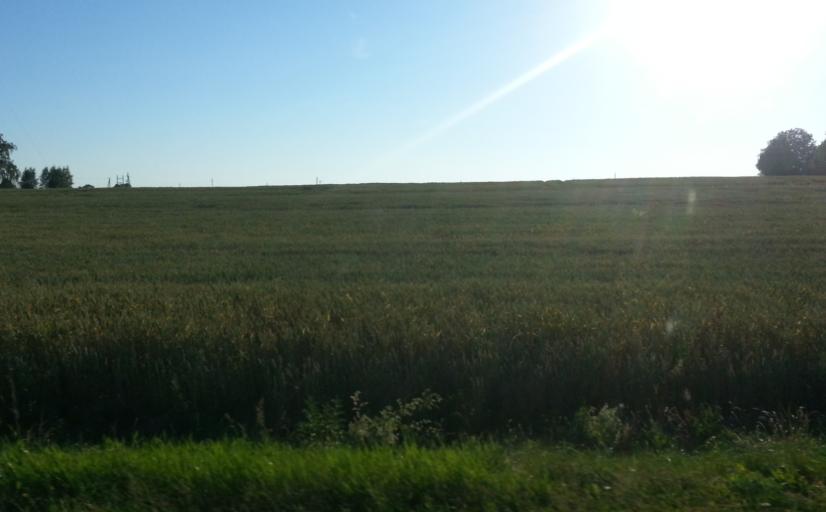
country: LT
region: Panevezys
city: Pasvalys
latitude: 55.9076
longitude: 24.3371
